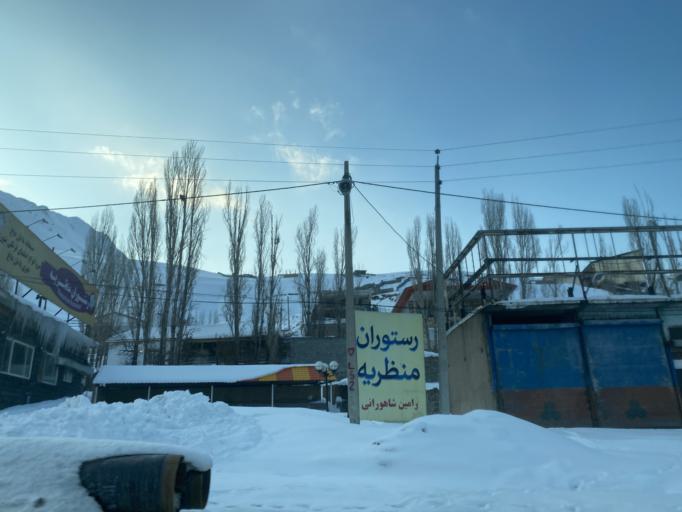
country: IR
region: Tehran
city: Damavand
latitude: 35.8319
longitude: 52.0329
